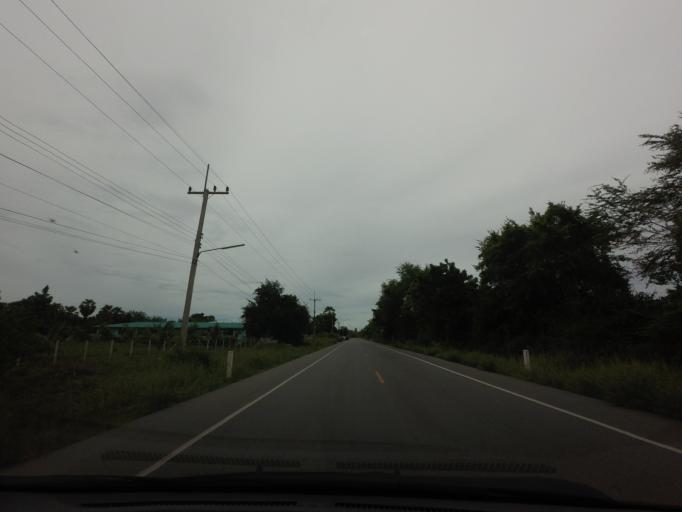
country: TH
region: Phetchaburi
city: Cha-am
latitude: 12.8431
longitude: 99.9887
